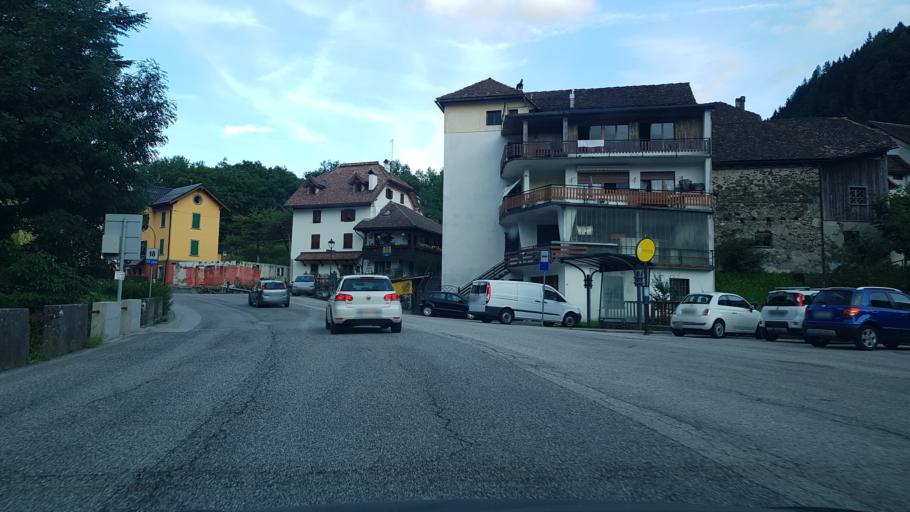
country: IT
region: Friuli Venezia Giulia
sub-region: Provincia di Udine
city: Rigolato
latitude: 46.5470
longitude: 12.8561
